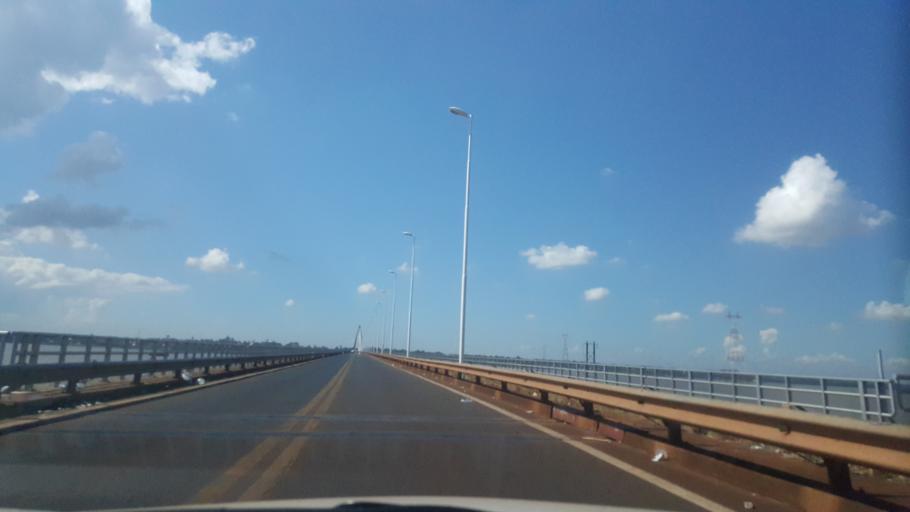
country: AR
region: Misiones
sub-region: Departamento de Capital
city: Posadas
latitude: -27.3761
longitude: -55.8797
